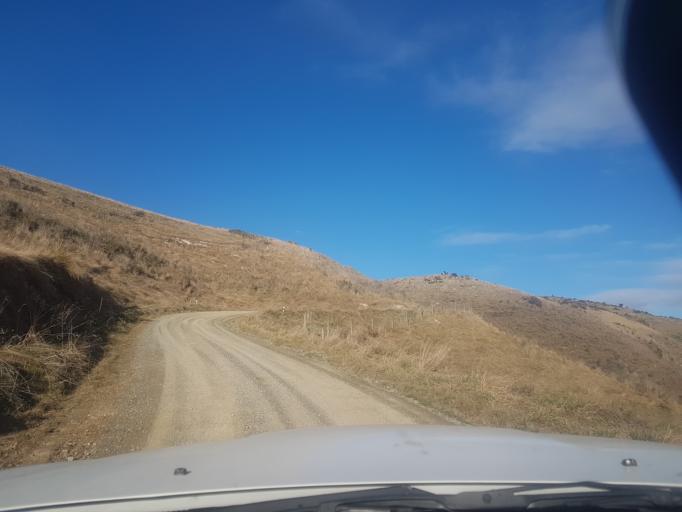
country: NZ
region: Canterbury
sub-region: Timaru District
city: Pleasant Point
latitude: -44.1729
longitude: 170.8836
